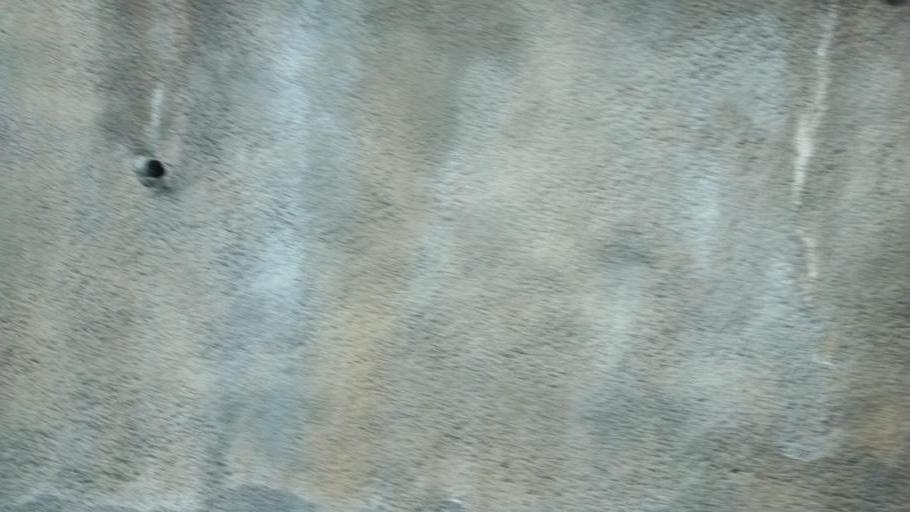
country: TW
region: Taiwan
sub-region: Taoyuan
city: Taoyuan
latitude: 24.9587
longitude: 121.3703
